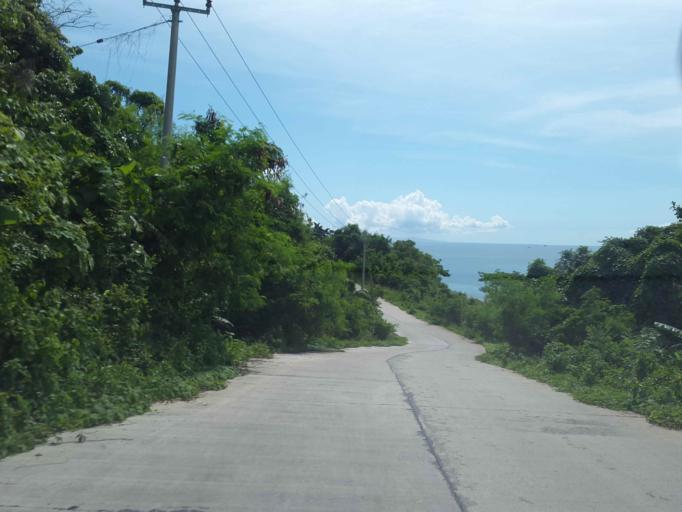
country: ID
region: Banten
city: Citeureup
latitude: -6.5096
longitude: 105.6368
